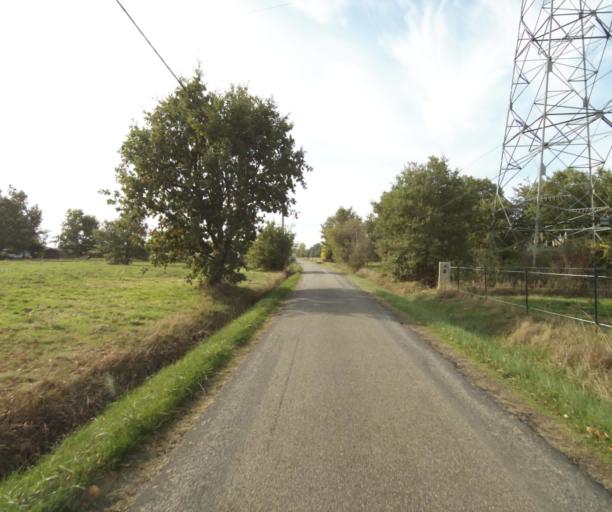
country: FR
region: Midi-Pyrenees
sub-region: Departement du Tarn-et-Garonne
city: Campsas
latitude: 43.9110
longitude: 1.3265
